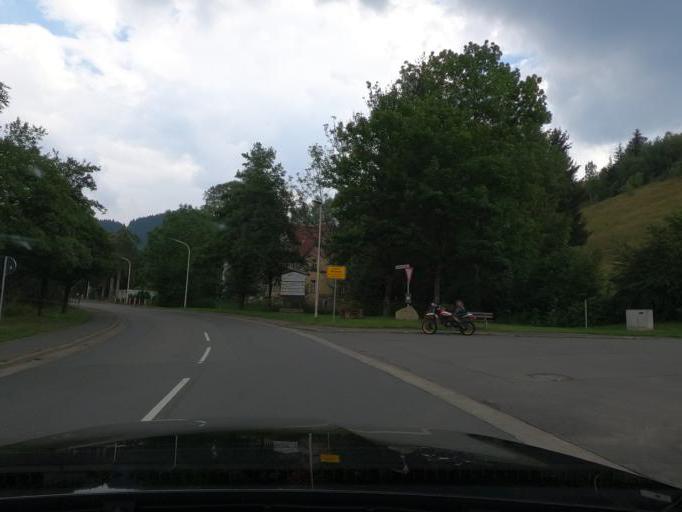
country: DE
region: Lower Saxony
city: Wildemann
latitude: 51.8277
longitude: 10.2744
